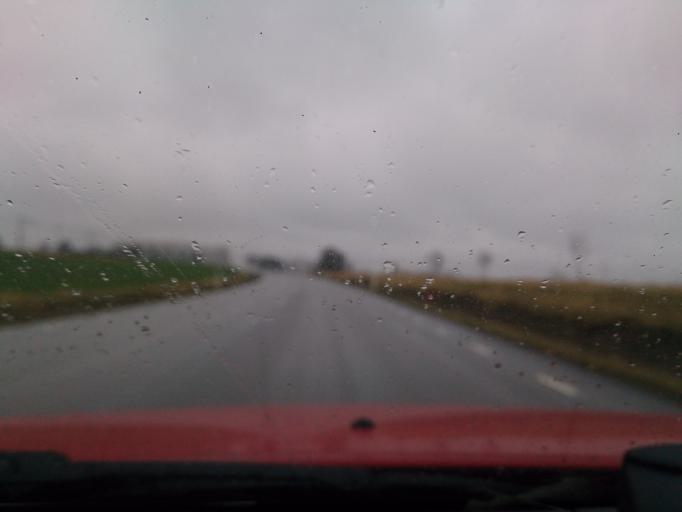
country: SE
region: Skane
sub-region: Ystads Kommun
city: Ystad
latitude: 55.4264
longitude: 13.7314
